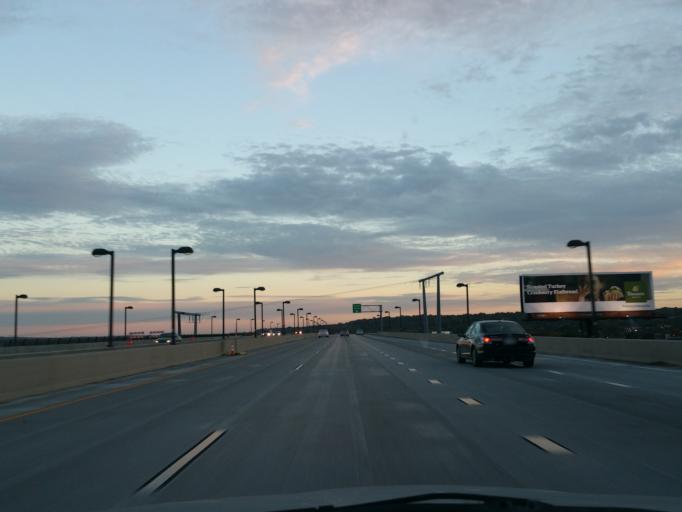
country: US
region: Minnesota
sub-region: Ramsey County
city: Saint Paul
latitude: 44.9494
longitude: -93.0808
